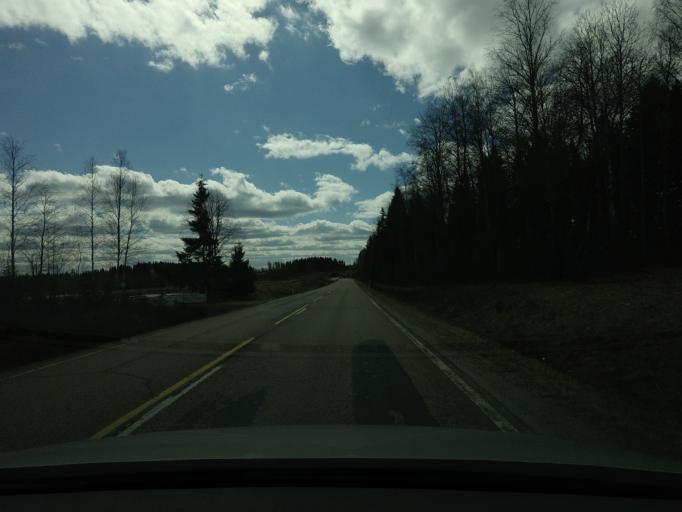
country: FI
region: South Karelia
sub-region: Lappeenranta
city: Taavetti
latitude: 60.9150
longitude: 27.5749
